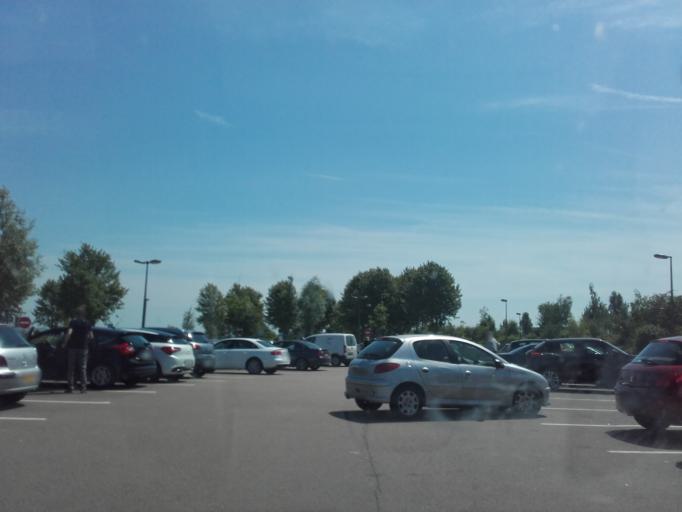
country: FR
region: Bourgogne
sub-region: Departement de l'Yonne
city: Avallon
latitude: 47.5033
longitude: 4.0367
